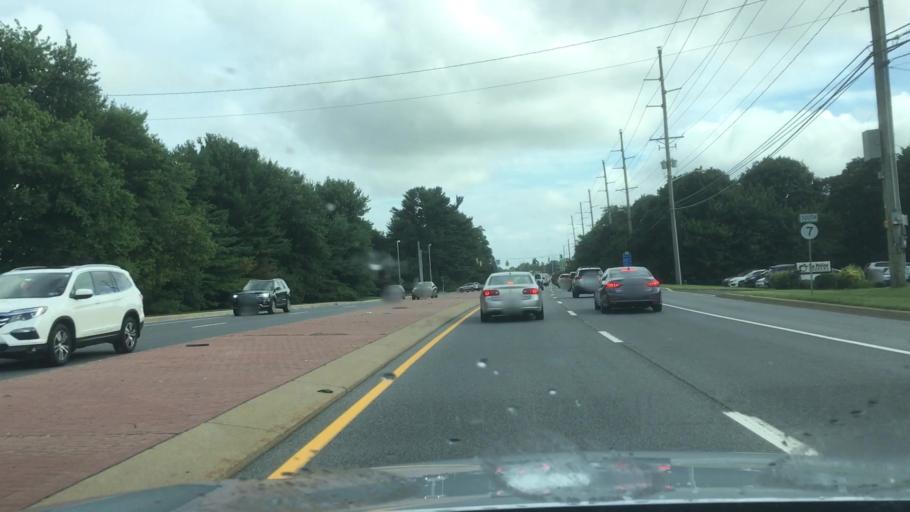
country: US
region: Delaware
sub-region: New Castle County
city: North Star
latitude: 39.7612
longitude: -75.7041
